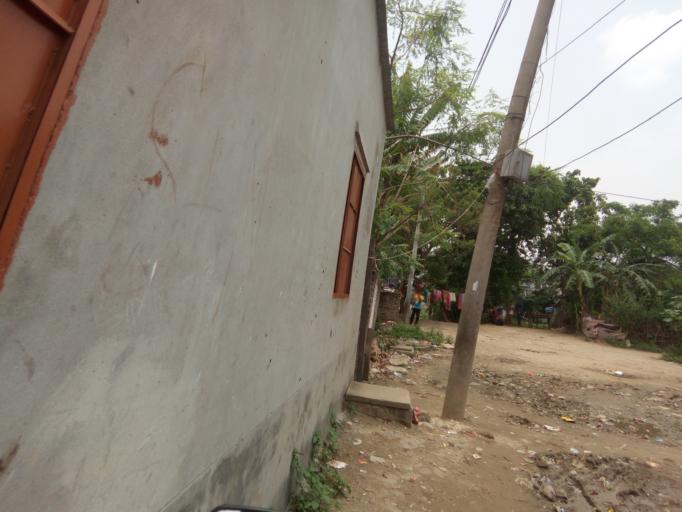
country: BD
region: Dhaka
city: Paltan
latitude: 23.7672
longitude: 90.4362
